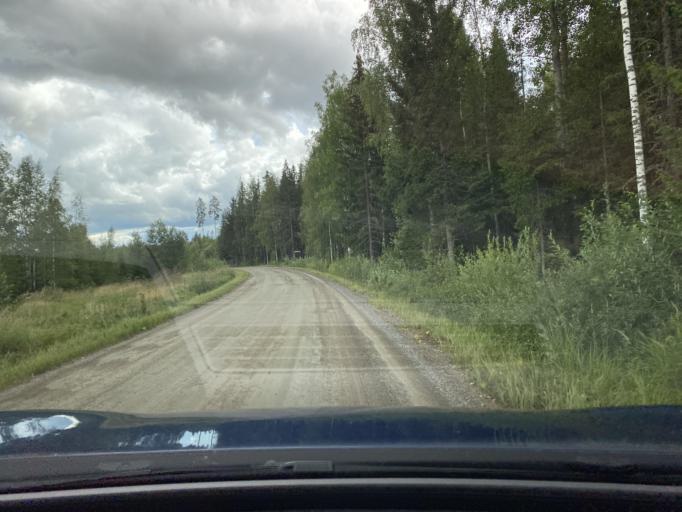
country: FI
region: Pirkanmaa
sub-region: Lounais-Pirkanmaa
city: Punkalaidun
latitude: 61.2219
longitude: 23.1612
